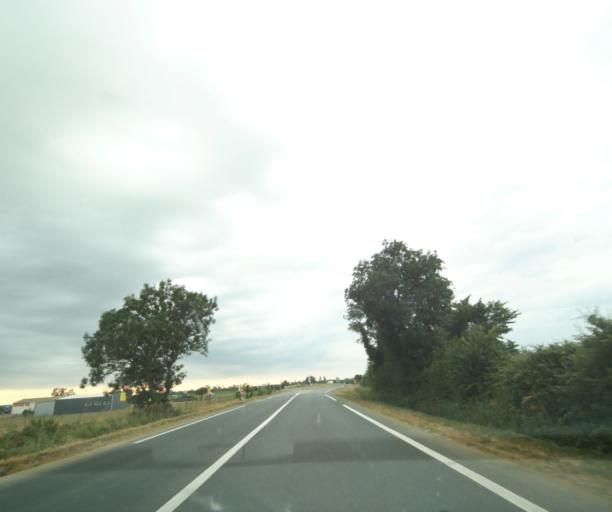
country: FR
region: Pays de la Loire
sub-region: Departement de la Vendee
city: Champagne-les-Marais
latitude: 46.4256
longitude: -1.0898
